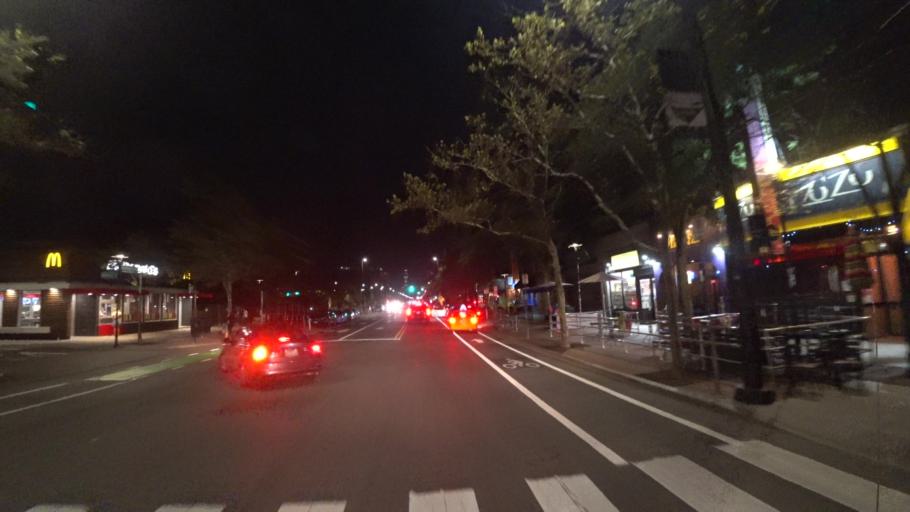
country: US
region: Massachusetts
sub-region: Middlesex County
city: Cambridge
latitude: 42.3640
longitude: -71.1014
